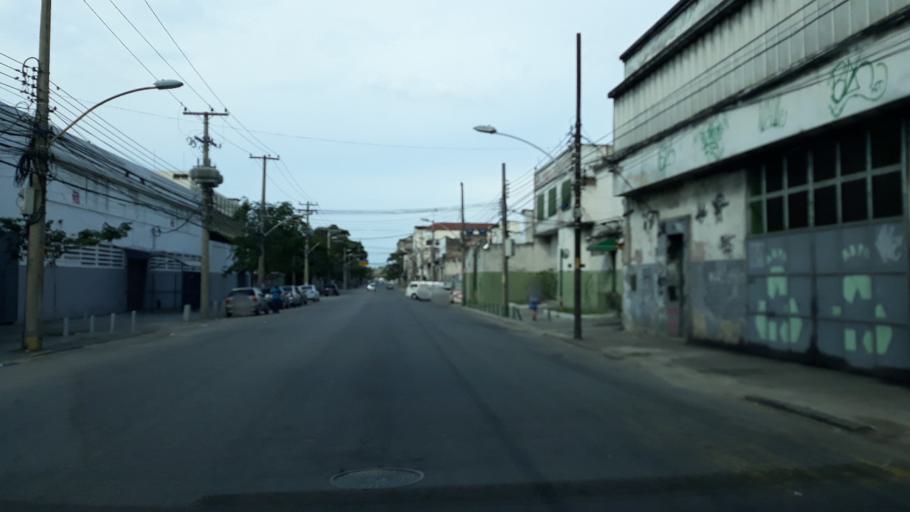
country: BR
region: Rio de Janeiro
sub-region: Rio De Janeiro
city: Rio de Janeiro
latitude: -22.8938
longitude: -43.2386
